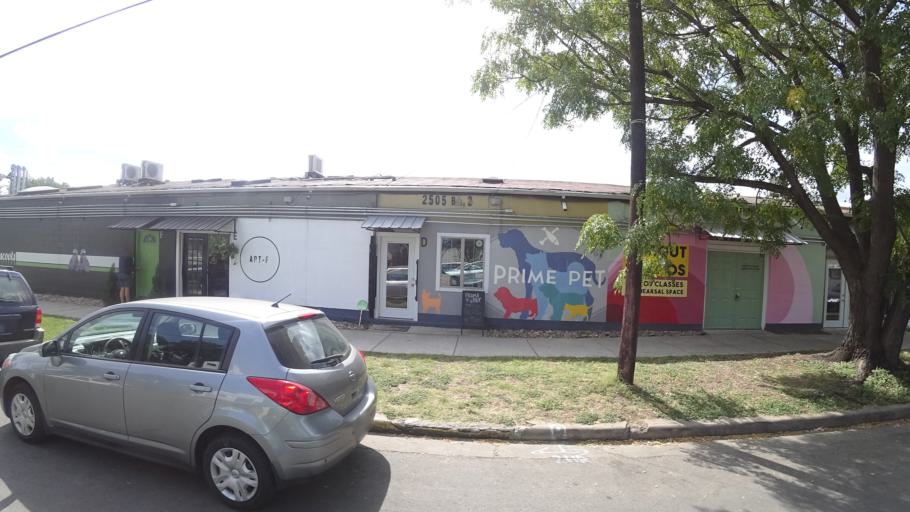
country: US
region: Texas
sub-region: Travis County
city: Austin
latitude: 30.2588
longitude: -97.7142
